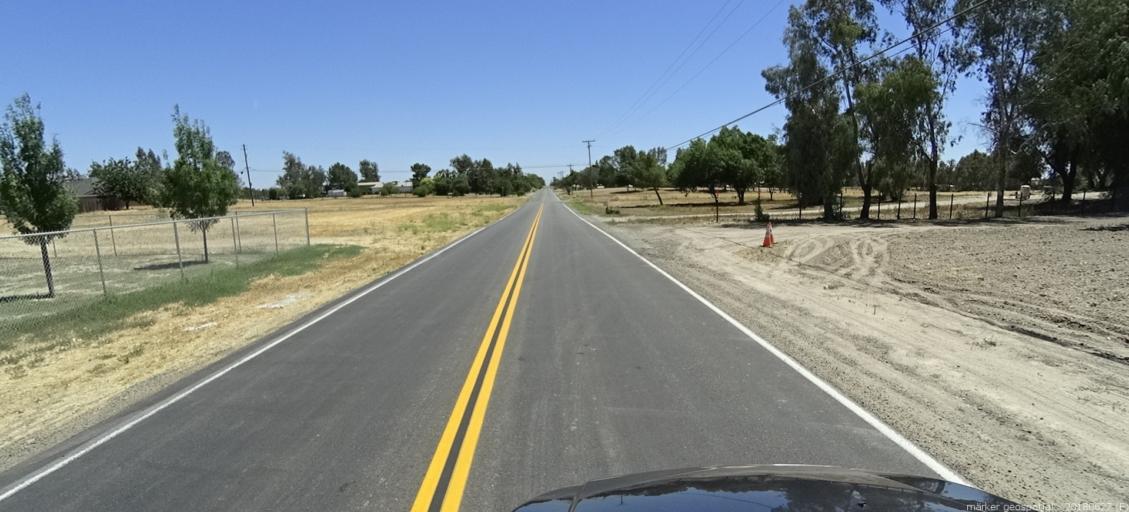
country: US
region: California
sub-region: Madera County
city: Bonadelle Ranchos-Madera Ranchos
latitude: 36.9628
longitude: -119.9119
